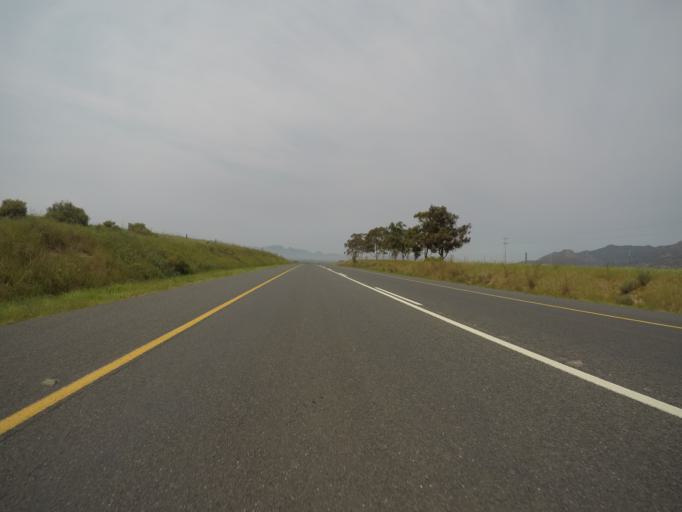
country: ZA
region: Western Cape
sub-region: West Coast District Municipality
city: Malmesbury
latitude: -33.5350
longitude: 18.8541
